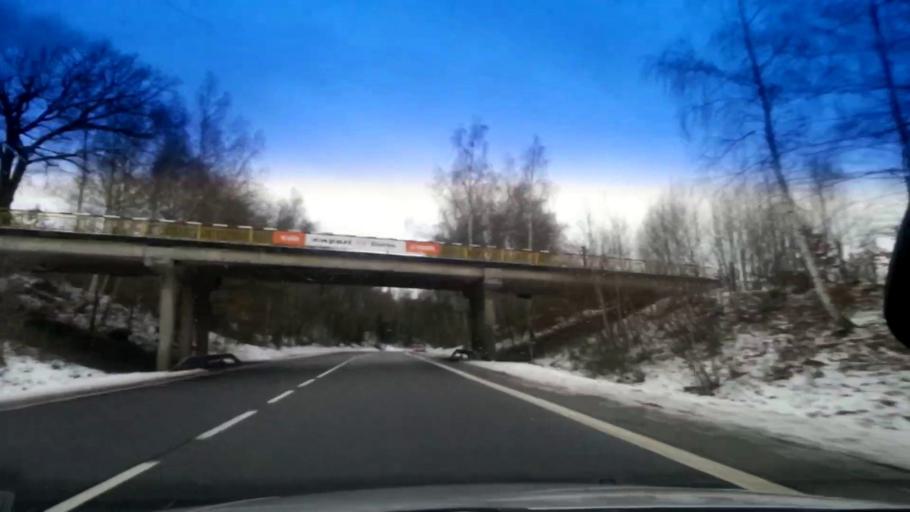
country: CZ
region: Karlovarsky
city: Hazlov
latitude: 50.1544
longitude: 12.2776
